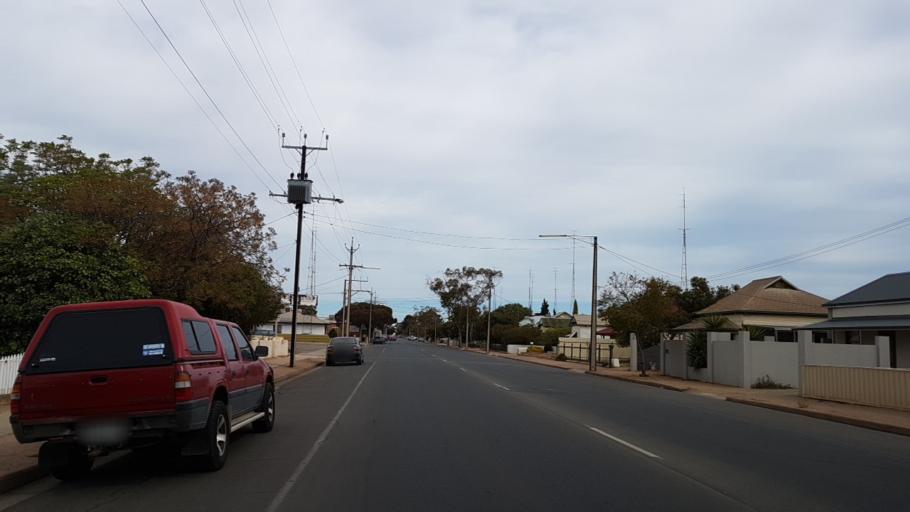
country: AU
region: South Australia
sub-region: Port Pirie City and Dists
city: Port Pirie
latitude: -33.1906
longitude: 138.0040
